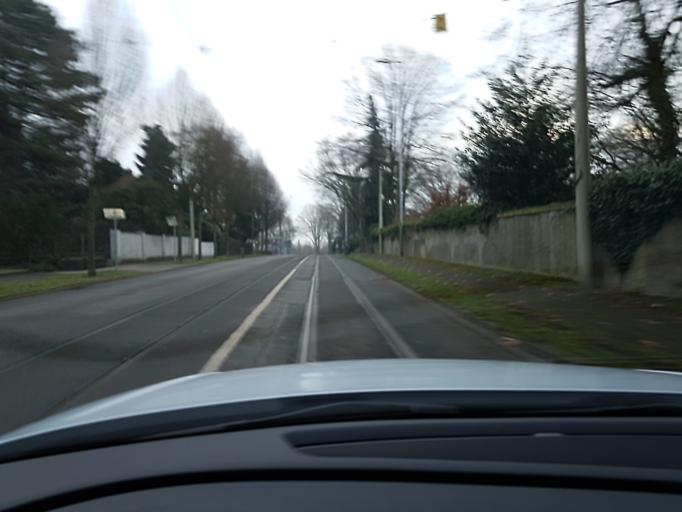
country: DE
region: North Rhine-Westphalia
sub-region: Regierungsbezirk Dusseldorf
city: Muelheim (Ruhr)
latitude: 51.4145
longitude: 6.8830
